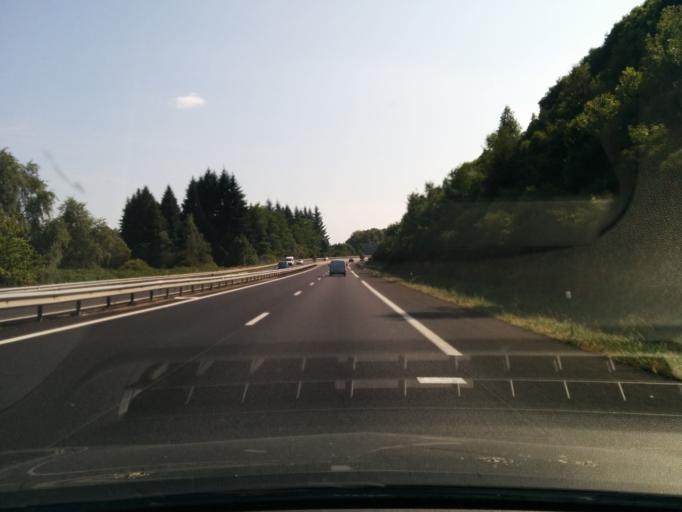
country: FR
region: Limousin
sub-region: Departement de la Haute-Vienne
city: Razes
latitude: 45.9968
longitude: 1.3371
